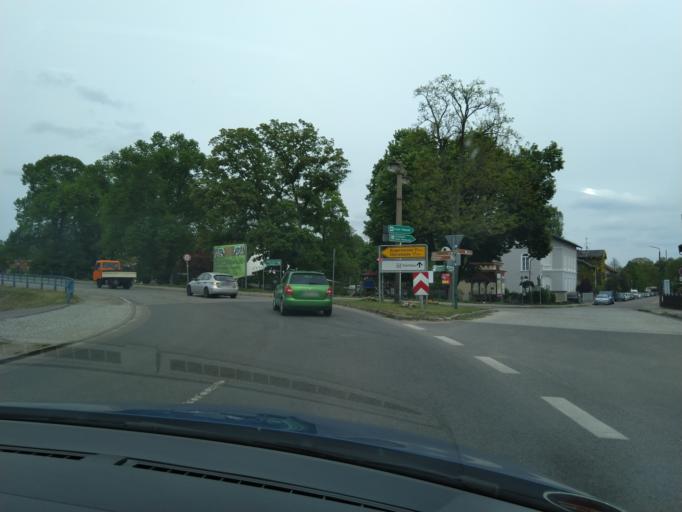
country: DE
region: Brandenburg
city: Oderberg
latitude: 52.8631
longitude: 14.0453
